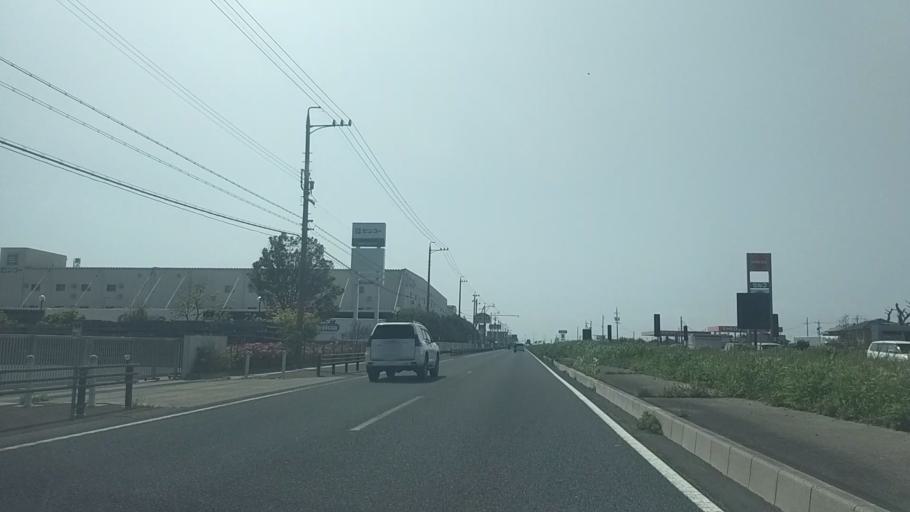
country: JP
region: Shizuoka
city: Hamamatsu
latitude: 34.6709
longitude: 137.7147
